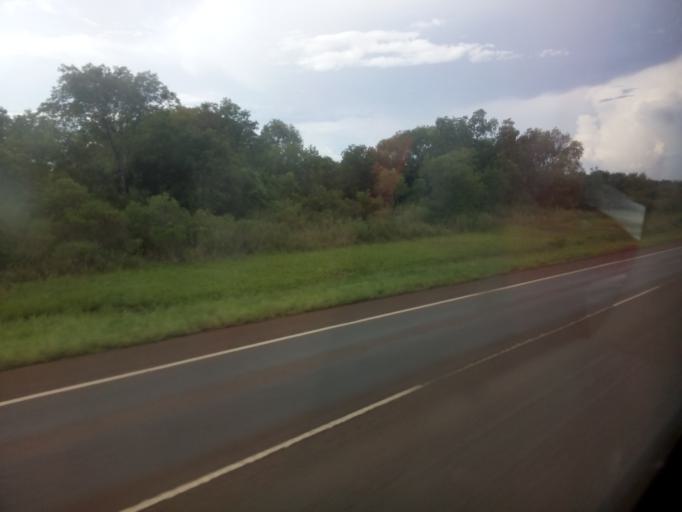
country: AR
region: Misiones
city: Santa Ana
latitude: -27.4078
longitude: -55.6056
